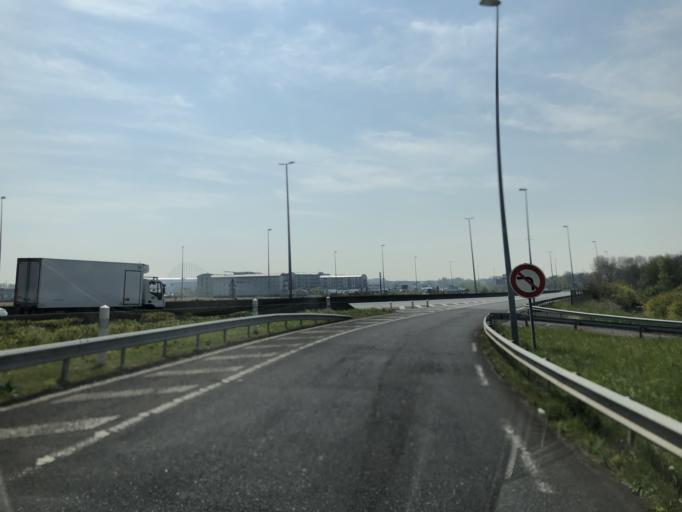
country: FR
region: Nord-Pas-de-Calais
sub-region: Departement du Pas-de-Calais
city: Coquelles
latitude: 50.9411
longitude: 1.8125
